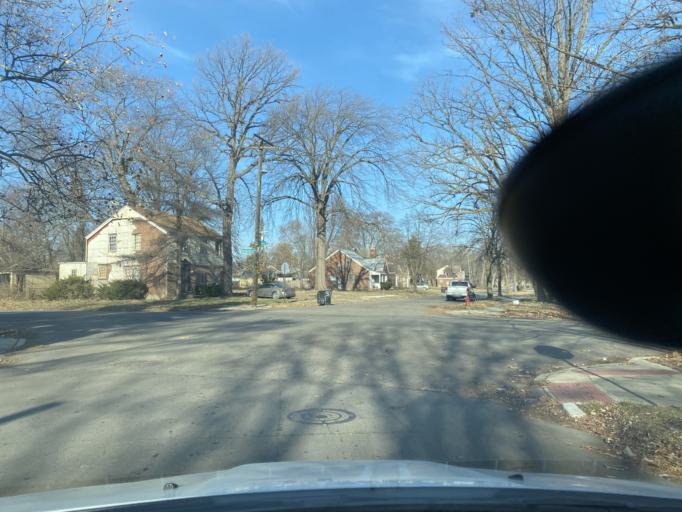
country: US
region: Michigan
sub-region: Wayne County
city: Grosse Pointe Park
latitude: 42.4095
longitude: -82.9525
